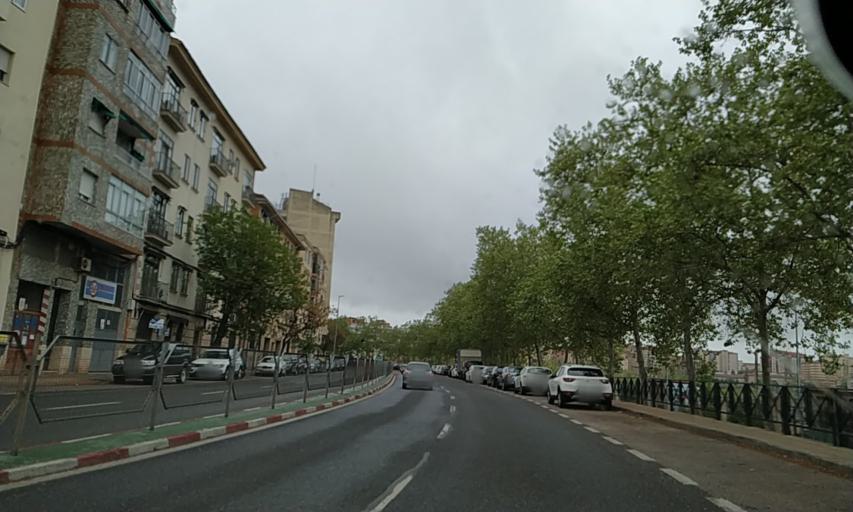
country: ES
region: Extremadura
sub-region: Provincia de Caceres
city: Caceres
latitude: 39.4777
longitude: -6.3792
